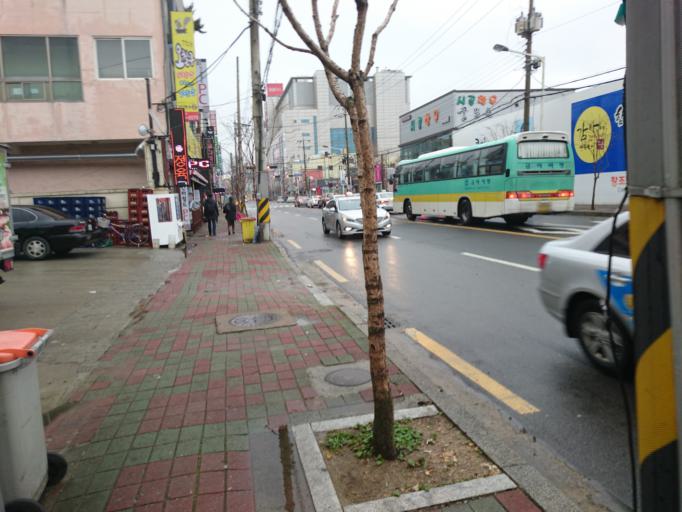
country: KR
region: Gyeongsangbuk-do
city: Enjitsu
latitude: 36.0143
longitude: 129.3470
